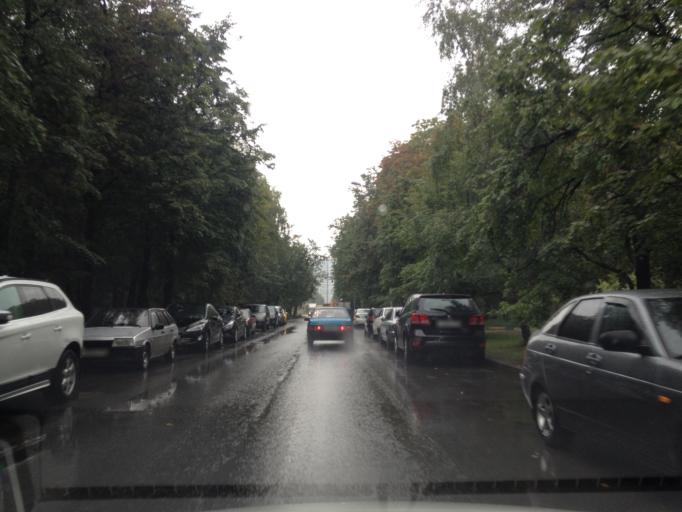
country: RU
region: Moskovskaya
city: Izmaylovo
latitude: 55.8010
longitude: 37.8053
